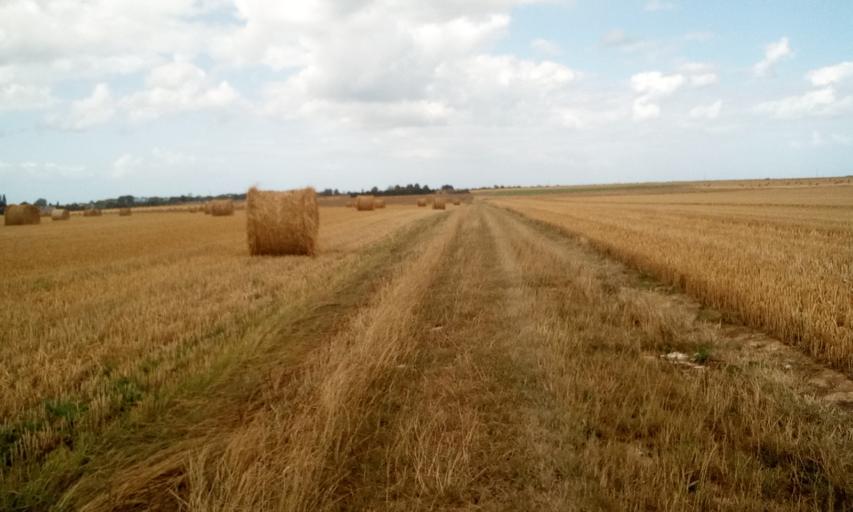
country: FR
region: Lower Normandy
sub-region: Departement du Calvados
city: Ver-sur-Mer
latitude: 49.3162
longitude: -0.5304
